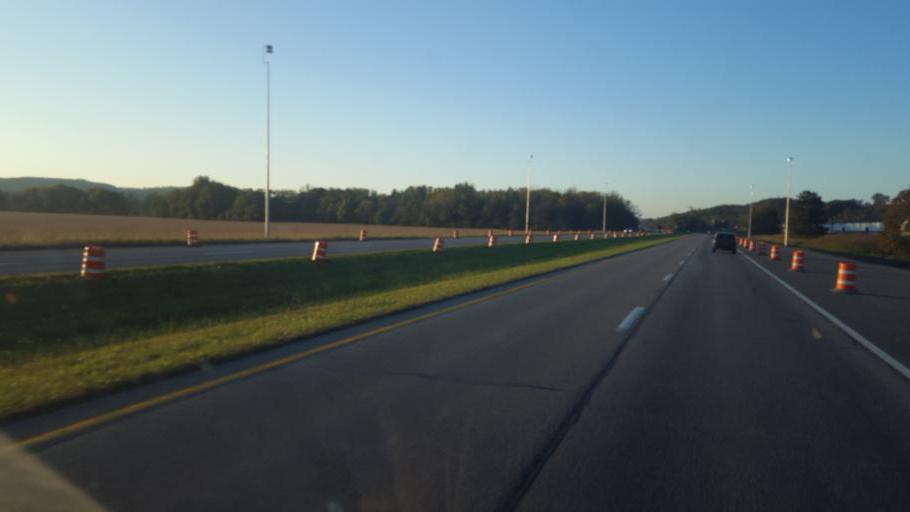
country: US
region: Ohio
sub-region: Scioto County
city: Lucasville
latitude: 38.8973
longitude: -83.0025
